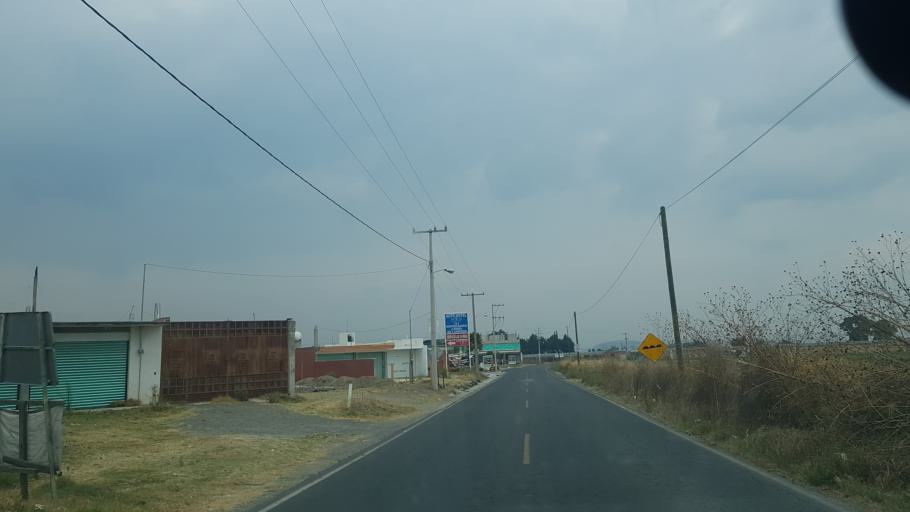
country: MX
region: Puebla
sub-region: Huejotzingo
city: San Mateo Capultitlan
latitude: 19.2023
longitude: -98.4333
